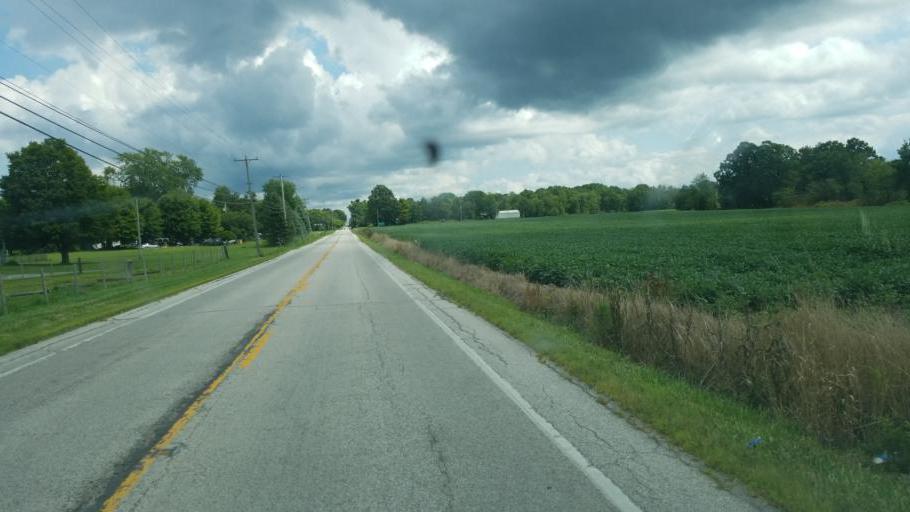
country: US
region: Ohio
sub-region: Ashtabula County
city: Andover
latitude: 41.6070
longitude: -80.6218
